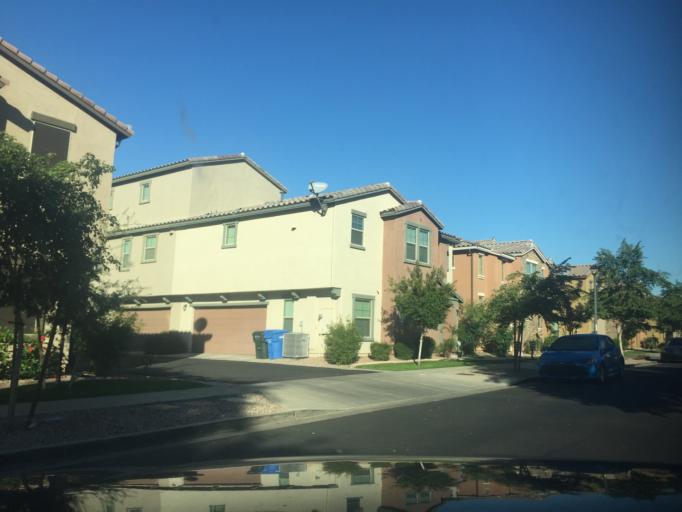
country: US
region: Arizona
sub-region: Maricopa County
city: Tolleson
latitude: 33.4671
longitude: -112.2262
